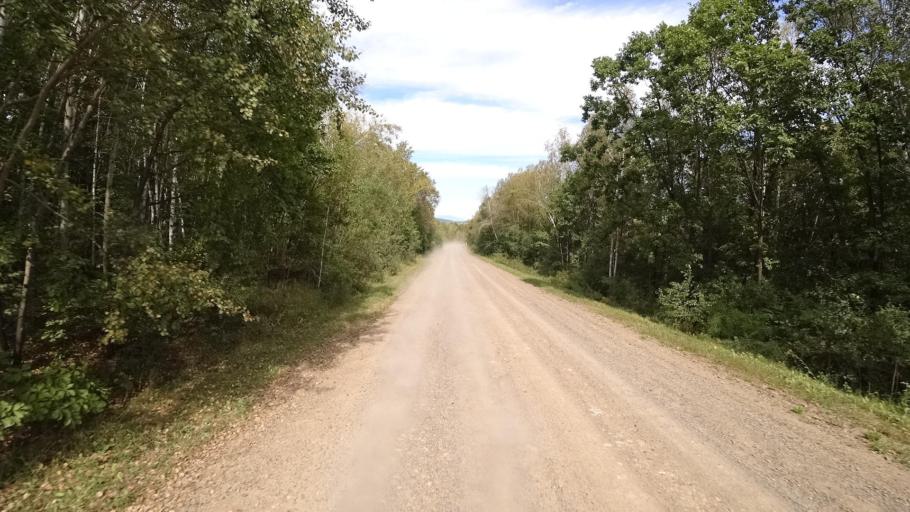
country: RU
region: Primorskiy
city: Yakovlevka
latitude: 44.6747
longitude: 133.6122
